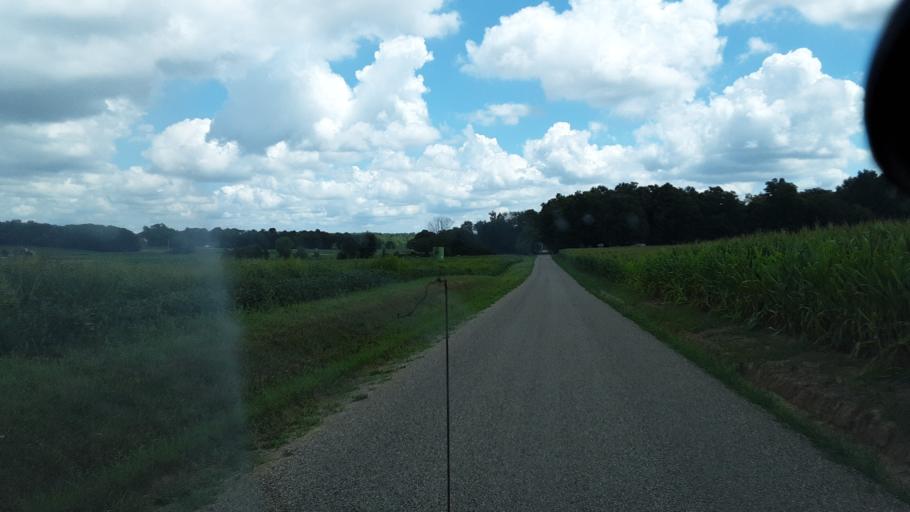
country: US
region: Ohio
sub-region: Licking County
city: Utica
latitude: 40.2617
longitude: -82.4078
